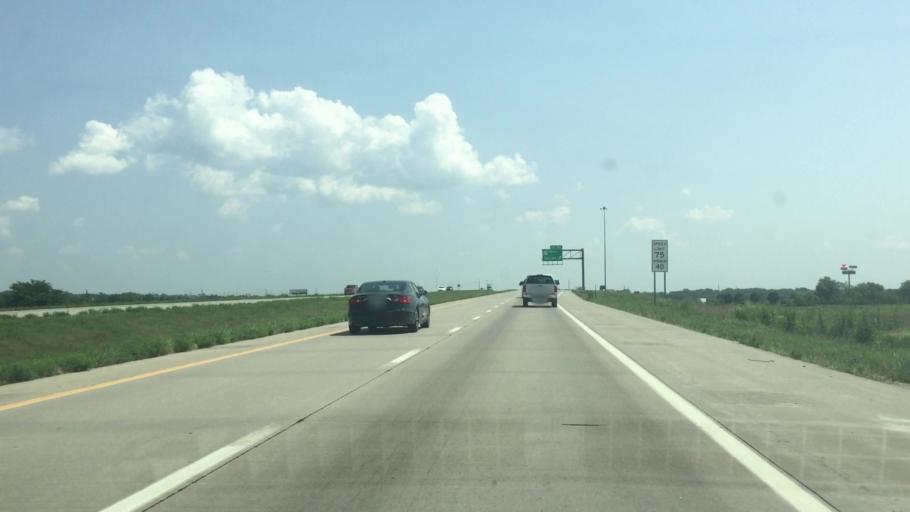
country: US
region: Kansas
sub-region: Franklin County
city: Ottawa
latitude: 38.5730
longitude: -95.2763
